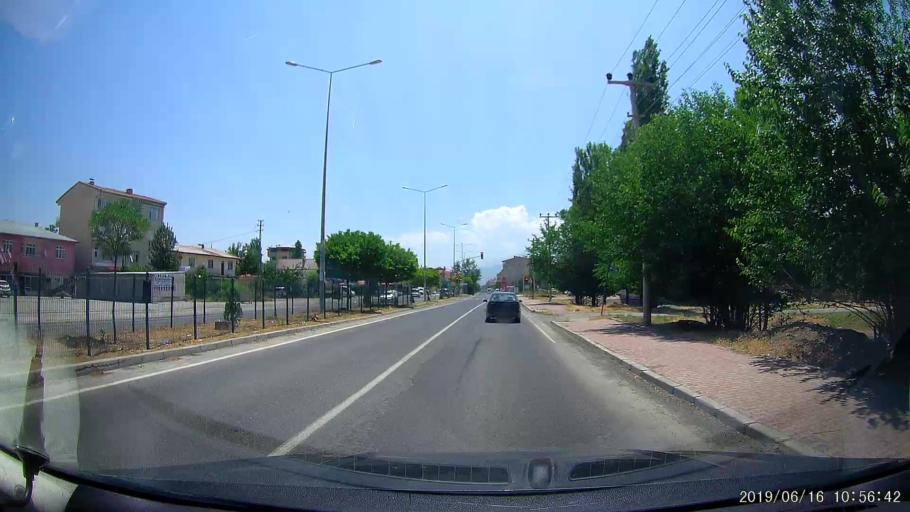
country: TR
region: Igdir
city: Igdir
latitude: 39.9279
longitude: 44.0255
